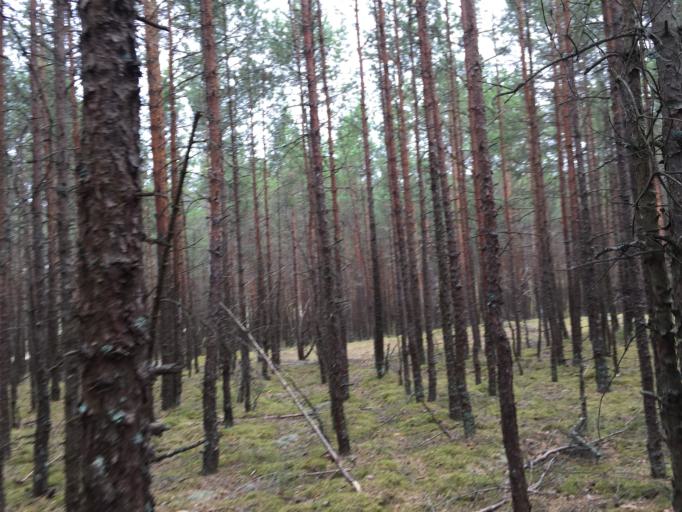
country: LV
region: Riga
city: Jaunciems
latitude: 57.1034
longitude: 24.1771
